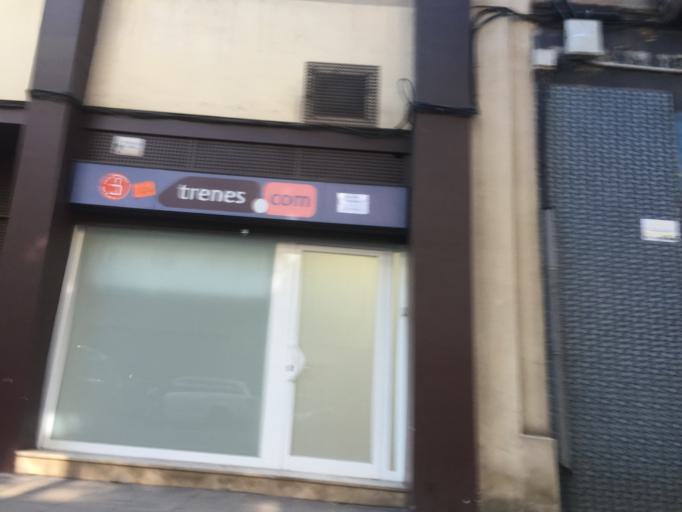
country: ES
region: Catalonia
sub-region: Provincia de Barcelona
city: Sant Andreu de Palomar
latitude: 41.4251
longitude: 2.1910
